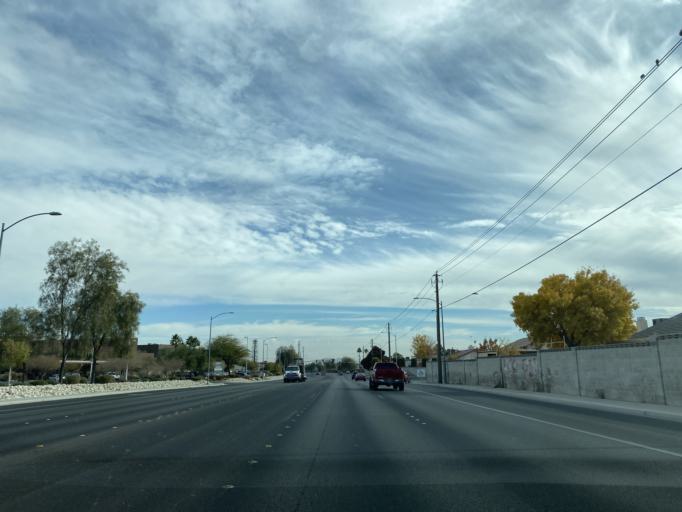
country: US
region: Nevada
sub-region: Clark County
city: Las Vegas
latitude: 36.2466
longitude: -115.2289
